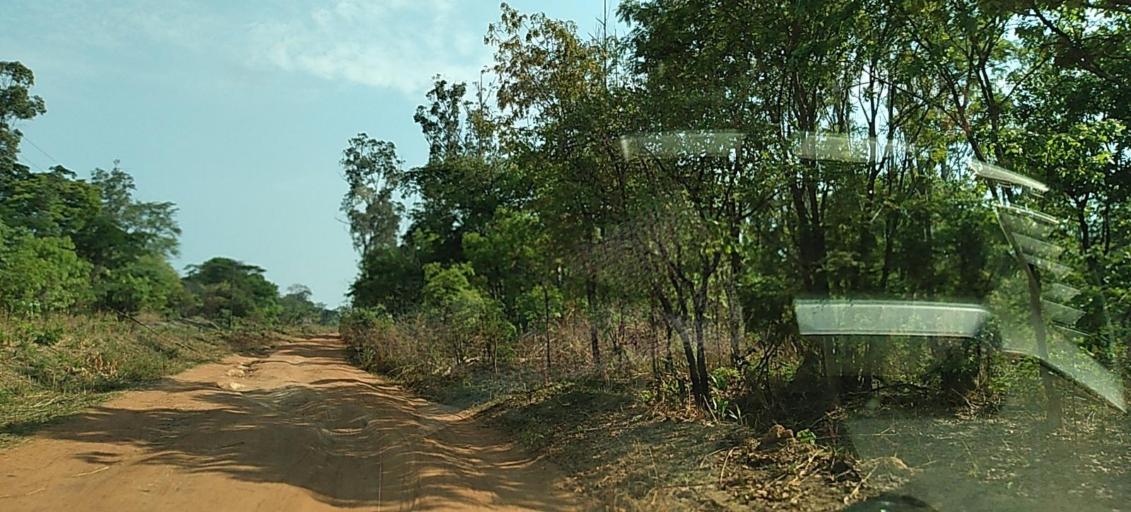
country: ZM
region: Copperbelt
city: Kalulushi
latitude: -13.0042
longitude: 27.8132
